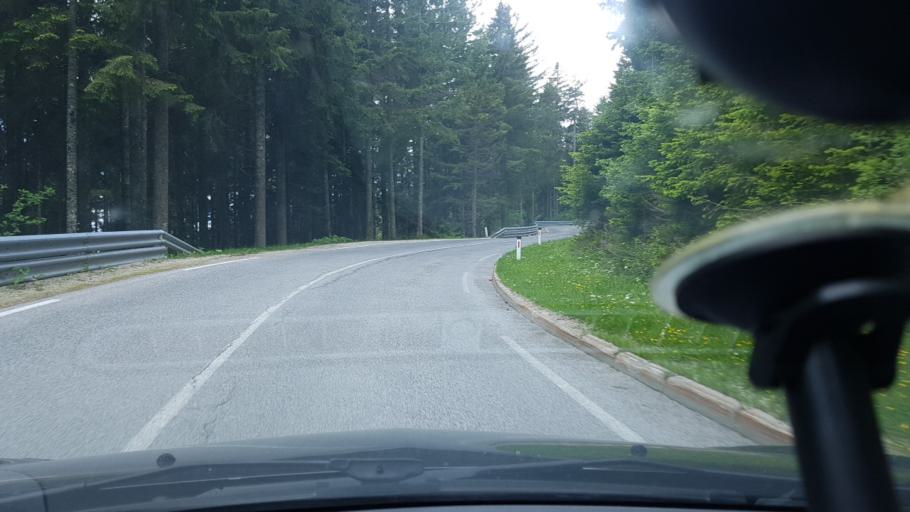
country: SI
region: Zrece
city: Zrece
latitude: 46.4485
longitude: 15.3401
